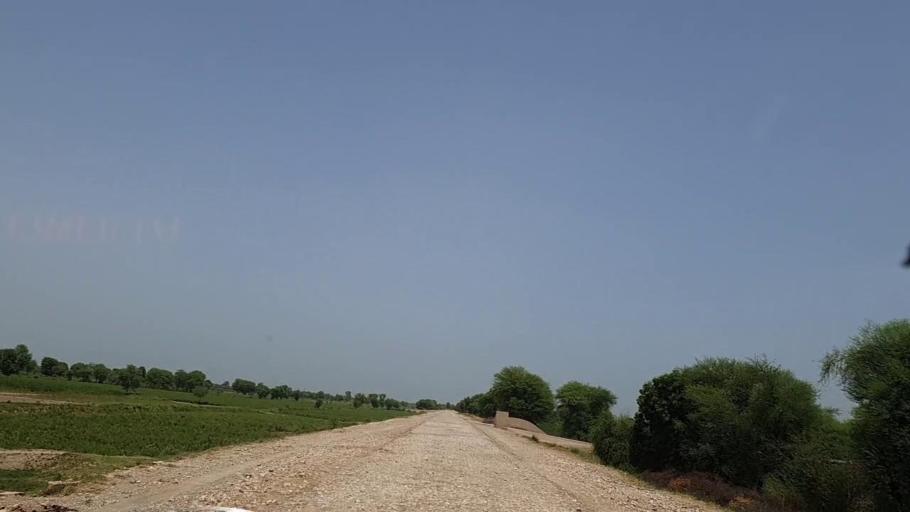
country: PK
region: Sindh
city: Tharu Shah
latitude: 27.0002
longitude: 68.0874
